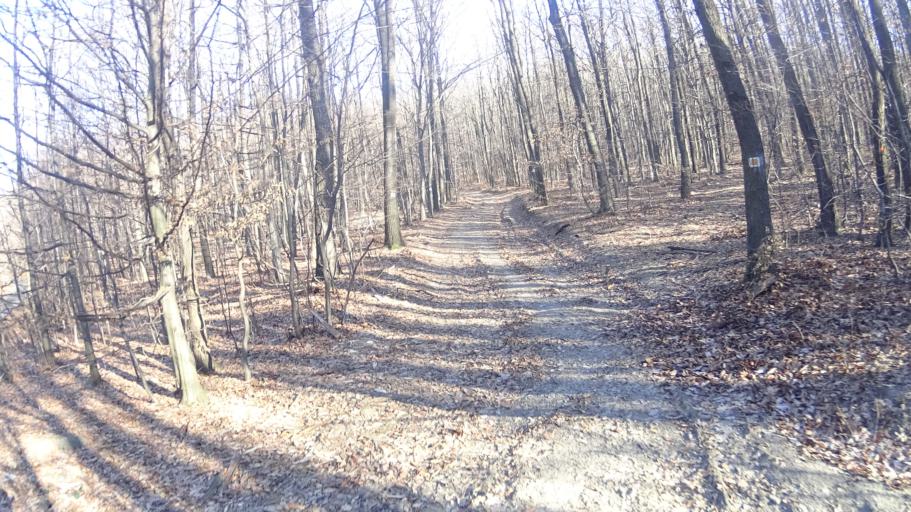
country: HU
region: Heves
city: Gyongyossolymos
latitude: 47.8601
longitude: 19.9551
